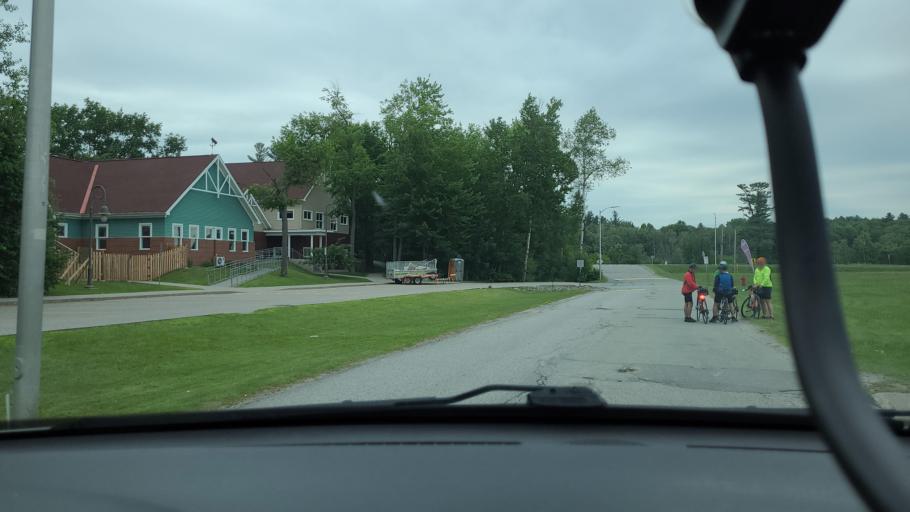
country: CA
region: Quebec
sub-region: Estrie
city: Sherbrooke
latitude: 45.3648
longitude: -71.8432
